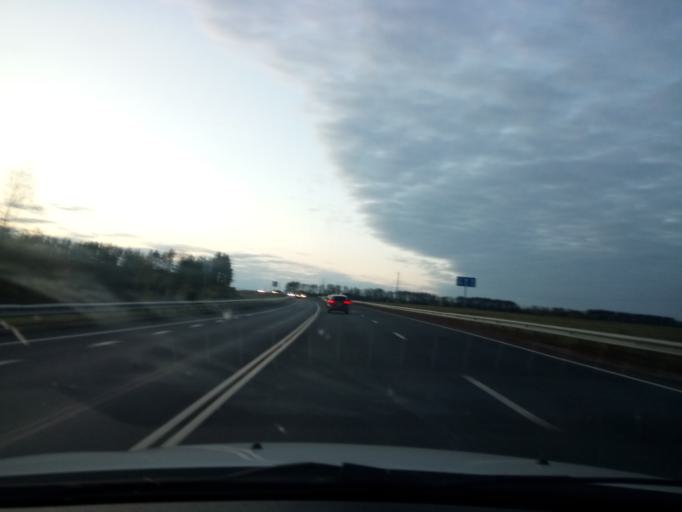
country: RU
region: Nizjnij Novgorod
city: Bol'shoye Murashkino
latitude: 55.8899
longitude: 44.7435
